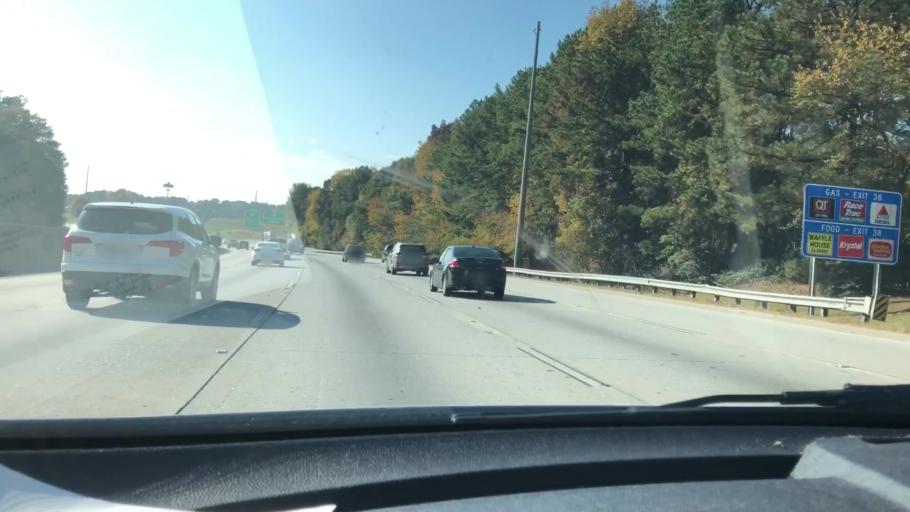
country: US
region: Georgia
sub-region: DeKalb County
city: Clarkston
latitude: 33.8325
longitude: -84.2522
